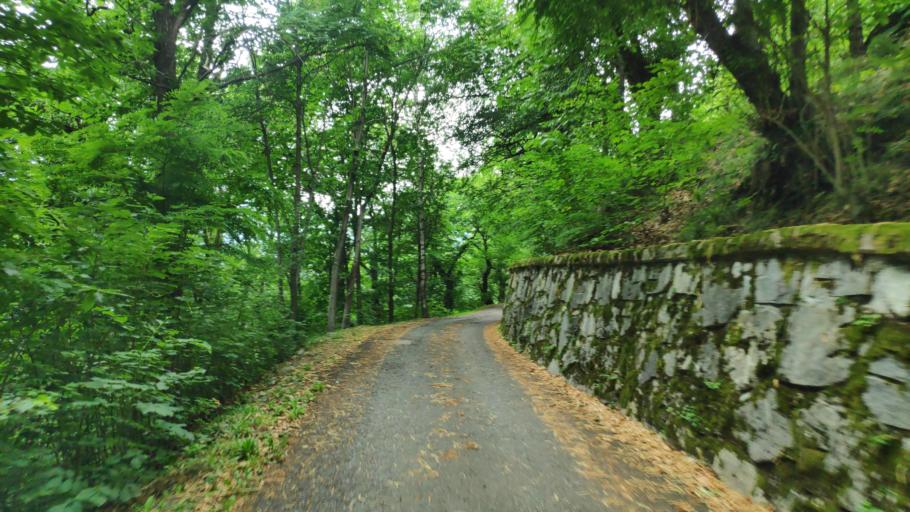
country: IT
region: Lombardy
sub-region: Provincia di Sondrio
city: Prata Camportaccio
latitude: 46.3005
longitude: 9.4026
